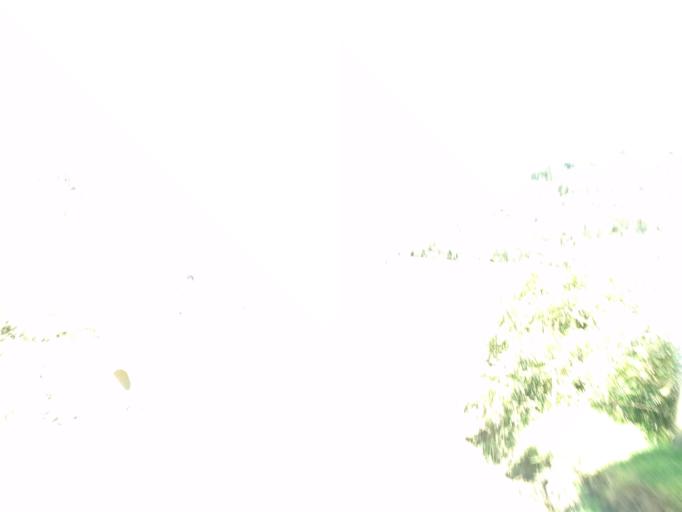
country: CO
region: Cauca
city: Jambalo
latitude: 2.7012
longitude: -76.3287
